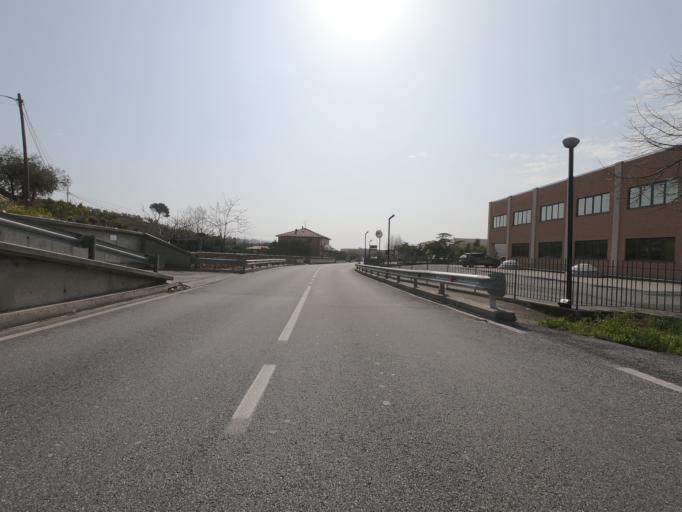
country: IT
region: Liguria
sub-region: Provincia di Savona
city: Cisano
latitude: 44.0754
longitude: 8.1599
